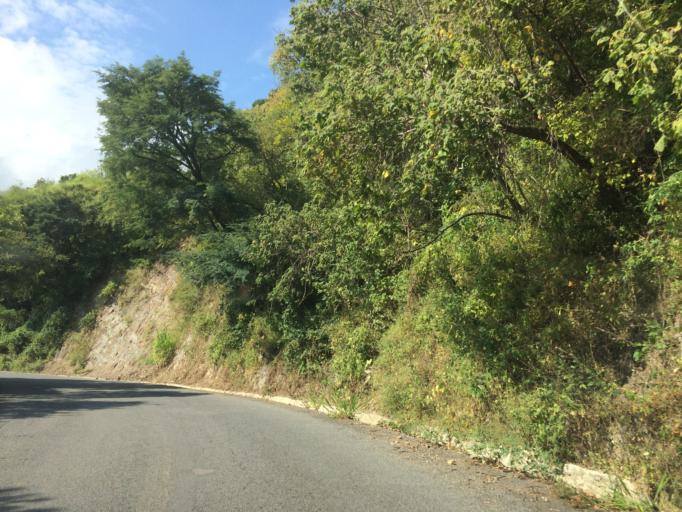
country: MX
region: Nayarit
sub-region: Ahuacatlan
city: Ahuacatlan
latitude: 21.0146
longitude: -104.4778
